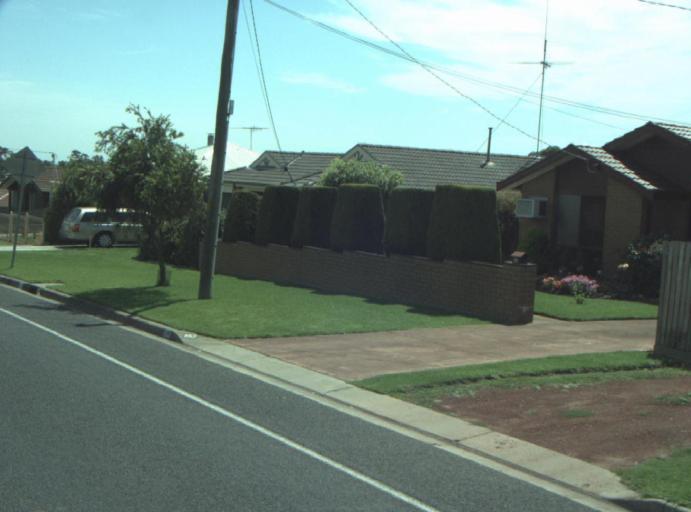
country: AU
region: Victoria
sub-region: Greater Geelong
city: Clifton Springs
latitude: -38.1579
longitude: 144.5737
